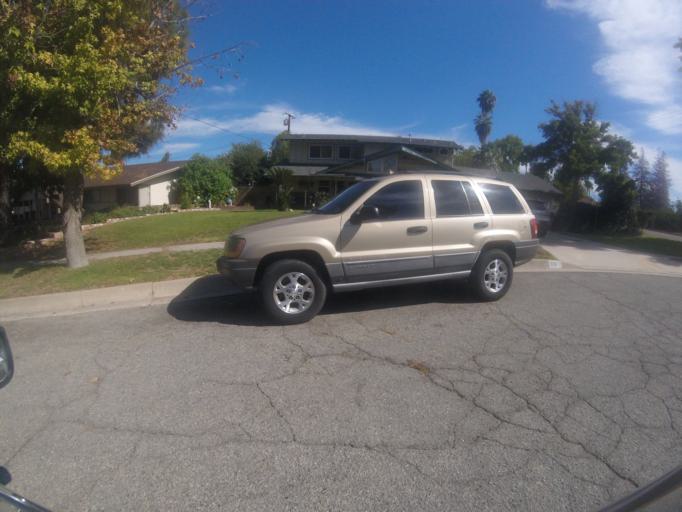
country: US
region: California
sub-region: San Bernardino County
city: Mentone
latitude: 34.0559
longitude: -117.1537
